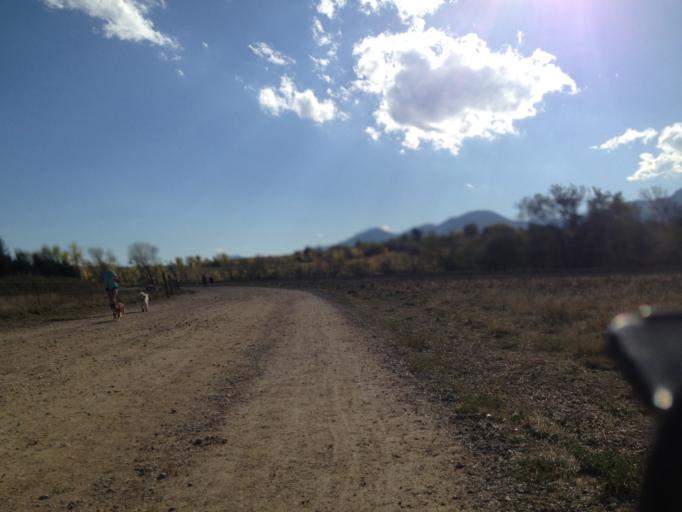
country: US
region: Colorado
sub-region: Boulder County
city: Boulder
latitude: 39.9811
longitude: -105.2335
